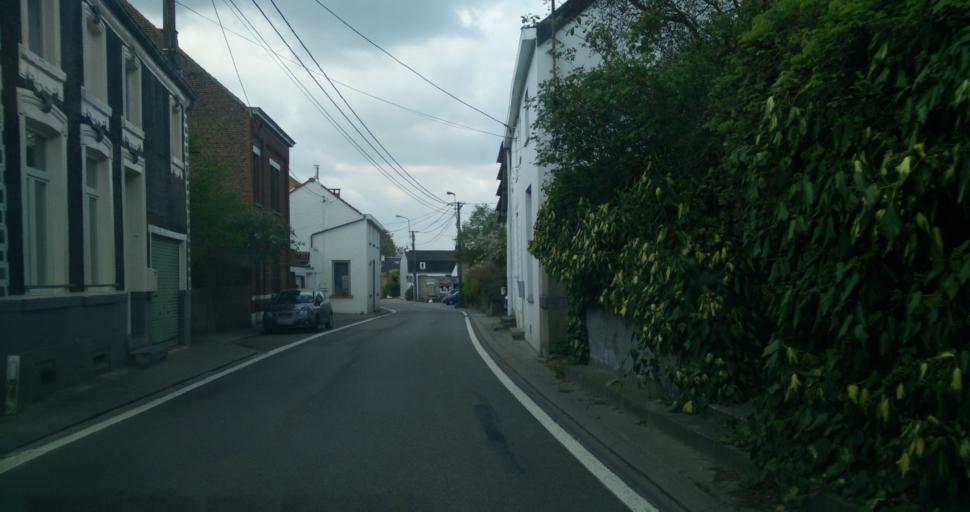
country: BE
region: Wallonia
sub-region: Province du Brabant Wallon
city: Ittre
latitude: 50.6537
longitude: 4.2967
